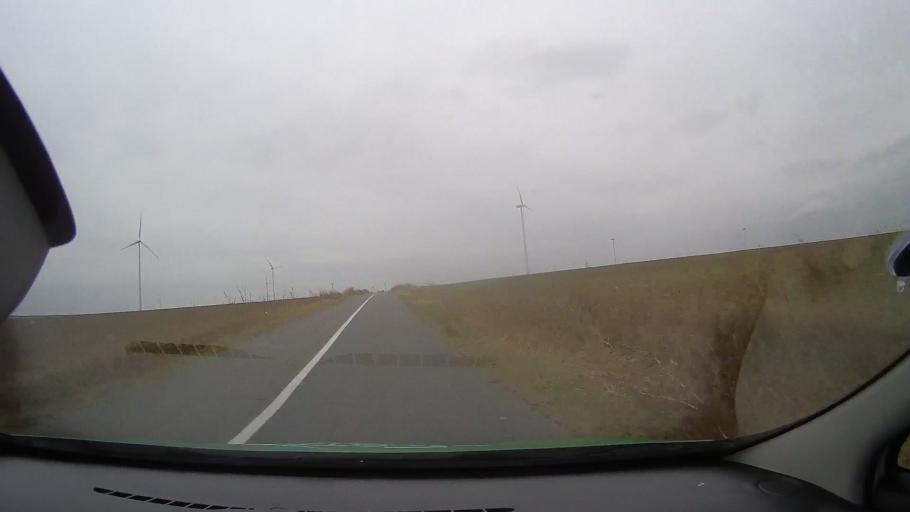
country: RO
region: Constanta
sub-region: Comuna Pantelimon
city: Pantelimon
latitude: 44.5034
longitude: 28.3500
